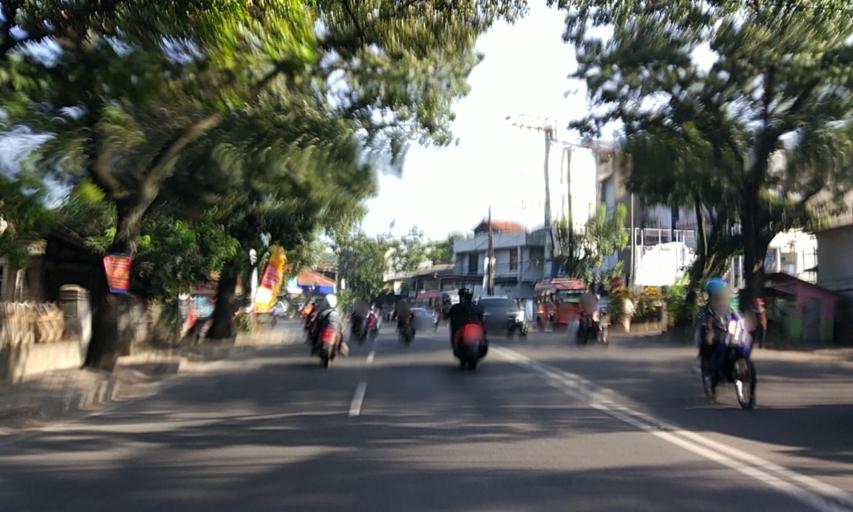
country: ID
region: West Java
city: Bandung
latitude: -6.9027
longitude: 107.6608
